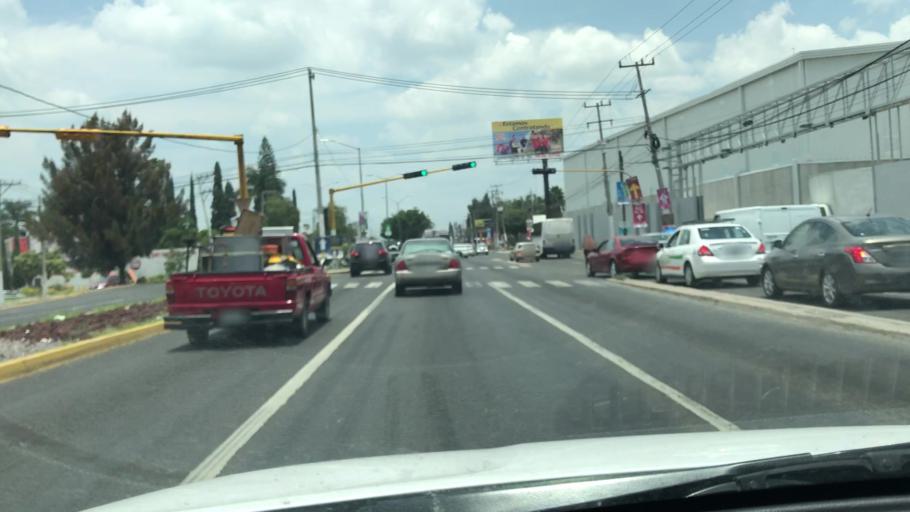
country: MX
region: Jalisco
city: Nuevo Mexico
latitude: 20.7486
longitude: -103.4175
